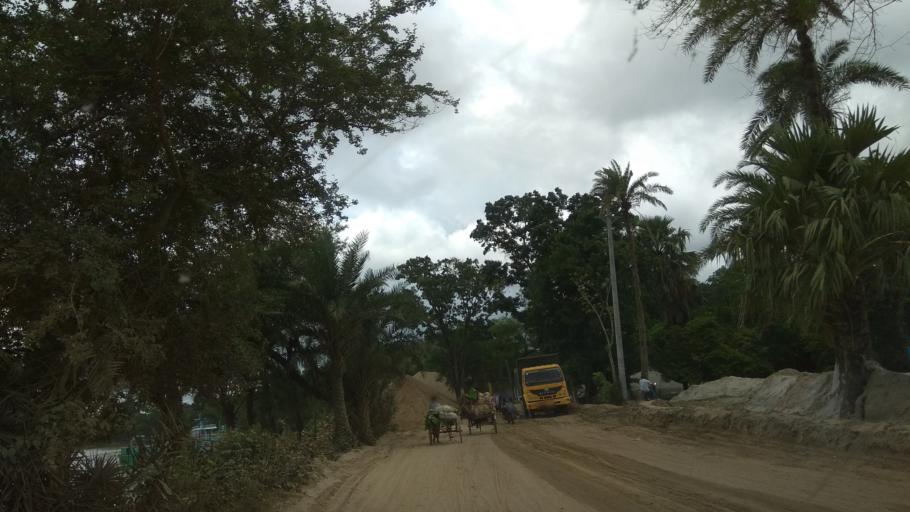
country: BD
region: Khulna
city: Kalia
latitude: 23.2057
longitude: 89.6987
